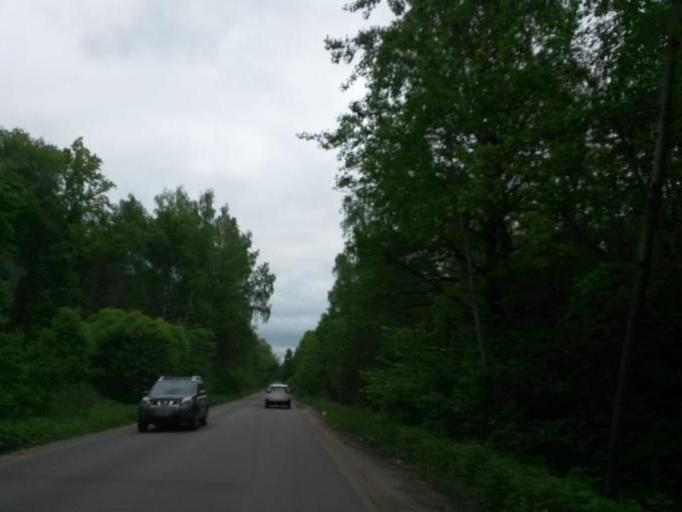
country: RU
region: Moskovskaya
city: Lyubuchany
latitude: 55.3082
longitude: 37.6154
